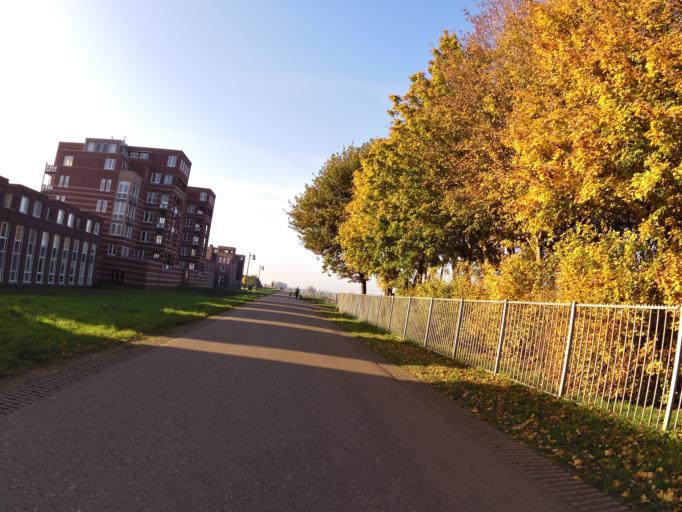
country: NL
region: Gelderland
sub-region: Gemeente Maasdriel
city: Hedel
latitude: 51.7295
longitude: 5.2582
